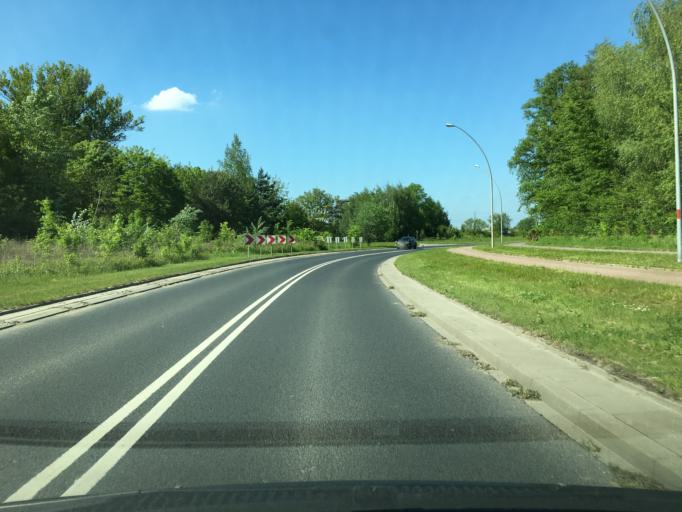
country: PL
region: Lower Silesian Voivodeship
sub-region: Powiat wroclawski
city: Bielany Wroclawskie
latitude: 51.0608
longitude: 16.9562
